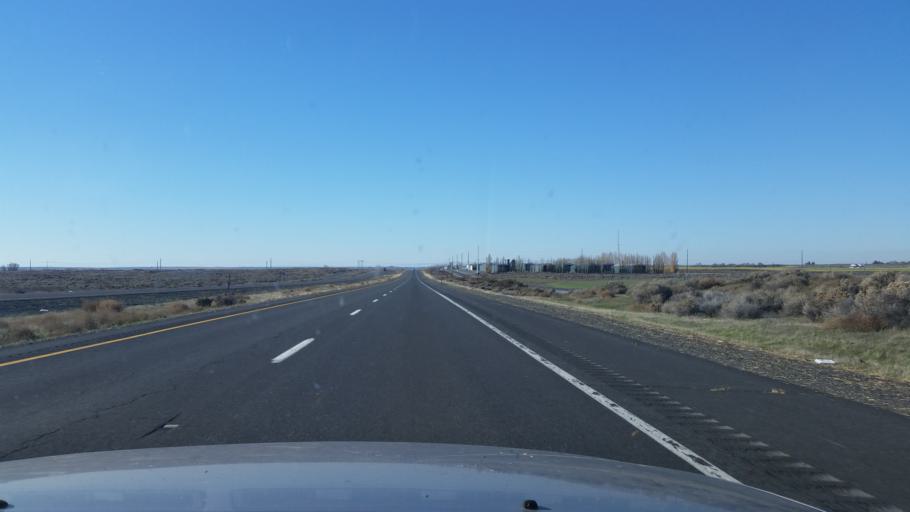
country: US
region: Washington
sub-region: Grant County
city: Cascade Valley
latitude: 47.1042
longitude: -119.3764
